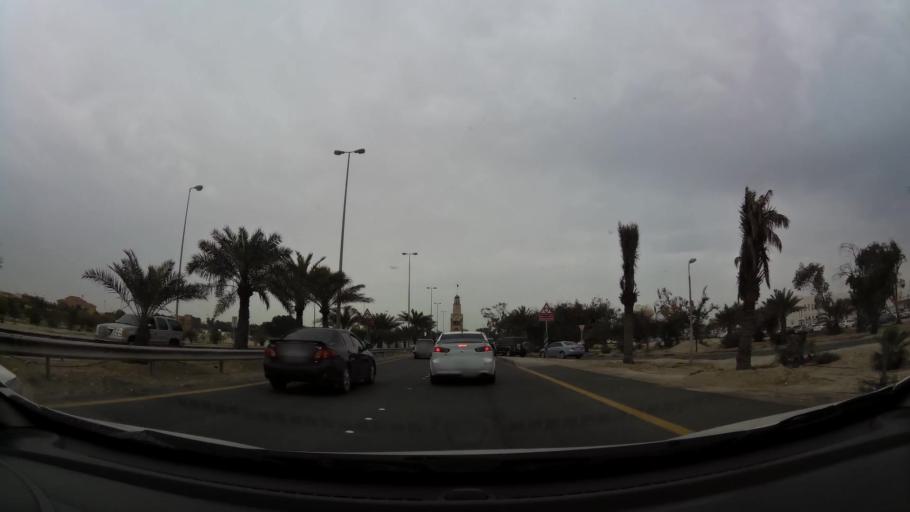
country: BH
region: Northern
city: Ar Rifa'
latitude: 26.1362
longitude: 50.5381
